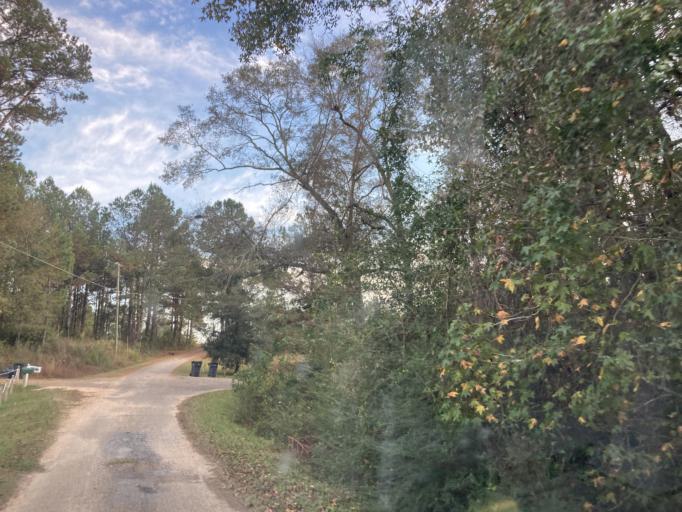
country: US
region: Mississippi
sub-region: Lamar County
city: Purvis
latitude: 31.1818
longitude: -89.3541
